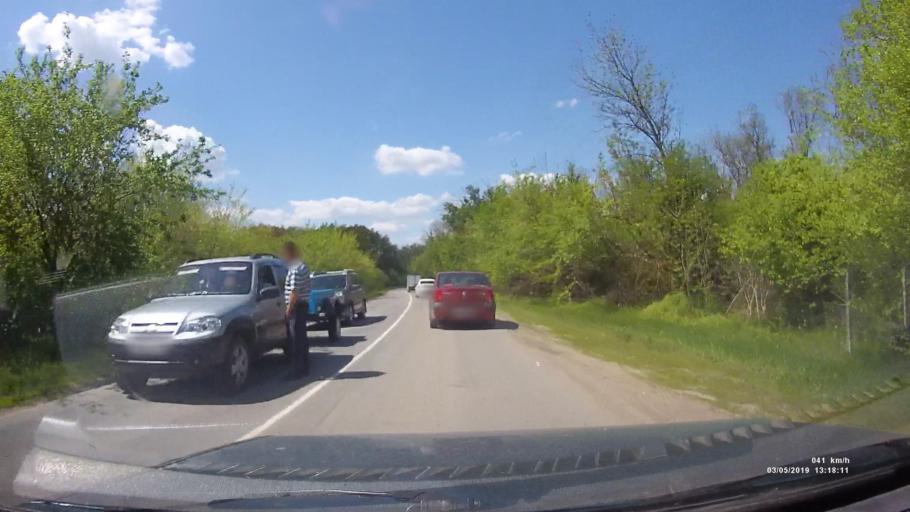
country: RU
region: Rostov
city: Semikarakorsk
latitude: 47.5315
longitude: 40.7498
